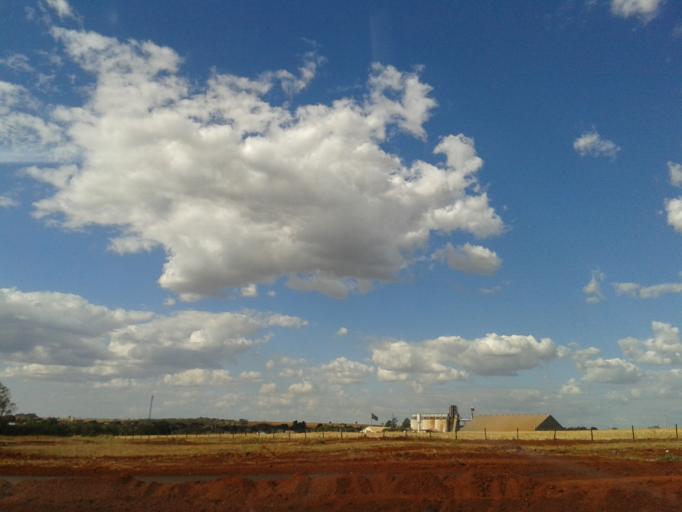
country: BR
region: Minas Gerais
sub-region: Capinopolis
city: Capinopolis
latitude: -18.6953
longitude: -49.5758
